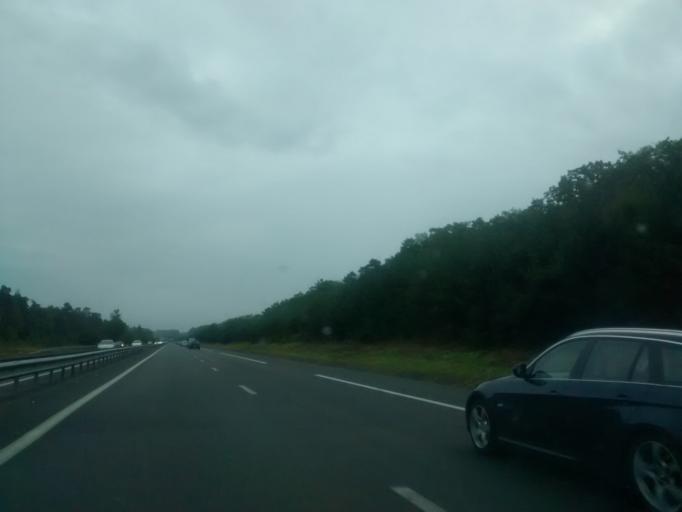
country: FR
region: Brittany
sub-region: Departement d'Ille-et-Vilaine
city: Liffre
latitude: 48.1910
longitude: -1.5432
